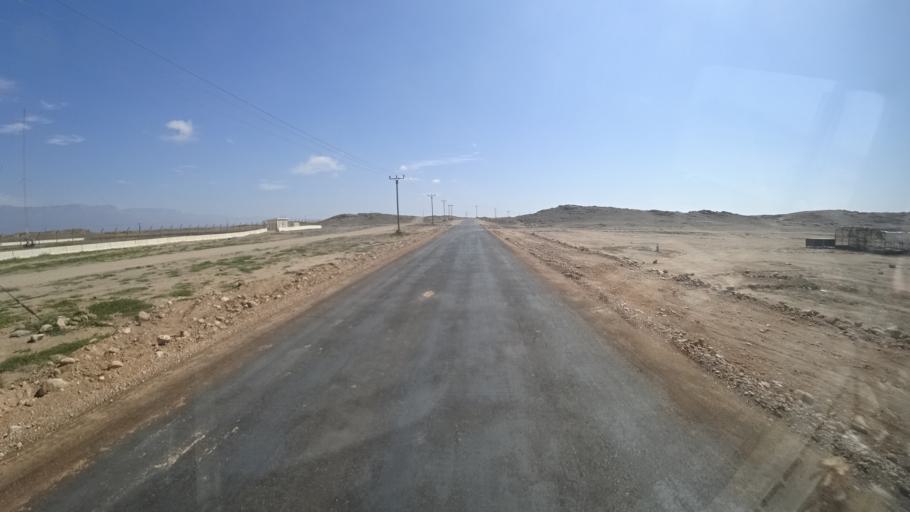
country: OM
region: Zufar
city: Salalah
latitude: 16.9658
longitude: 54.7498
